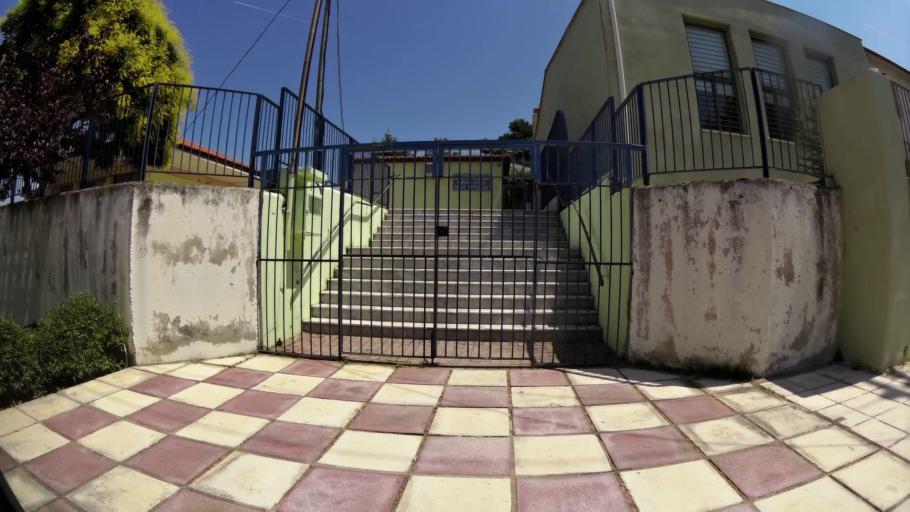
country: GR
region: Central Macedonia
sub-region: Nomos Thessalonikis
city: Nea Michaniona
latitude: 40.4754
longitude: 22.8665
